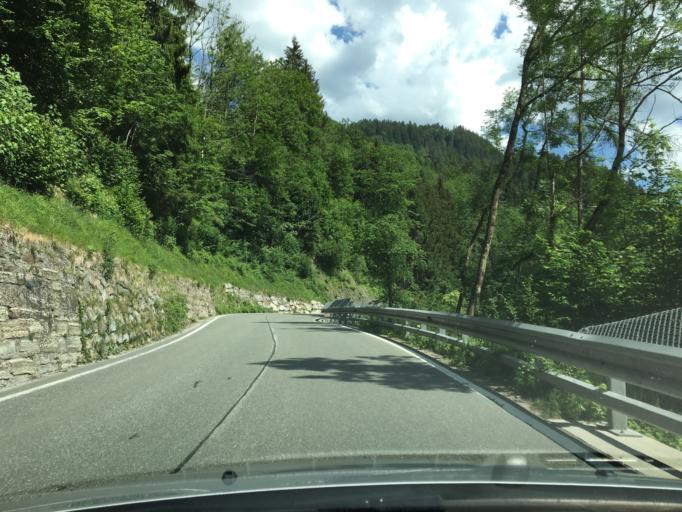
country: AT
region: Salzburg
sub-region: Politischer Bezirk Sankt Johann im Pongau
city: Sankt Johann im Pongau
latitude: 47.3434
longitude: 13.2089
